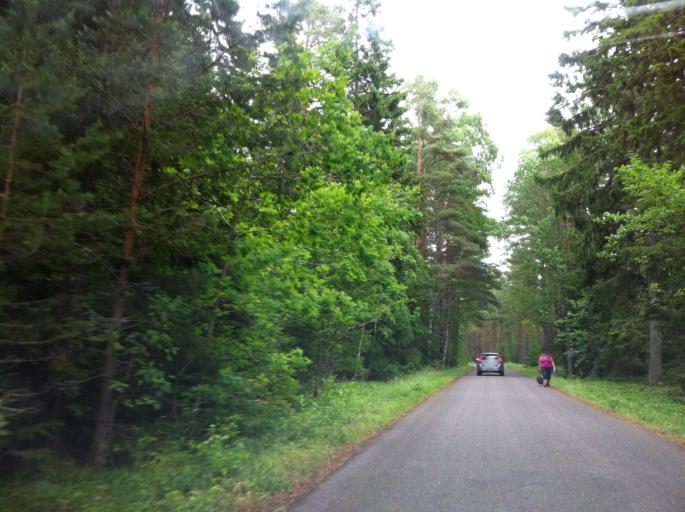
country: SE
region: Kalmar
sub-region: Vasterviks Kommun
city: Vaestervik
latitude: 57.3323
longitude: 17.1029
